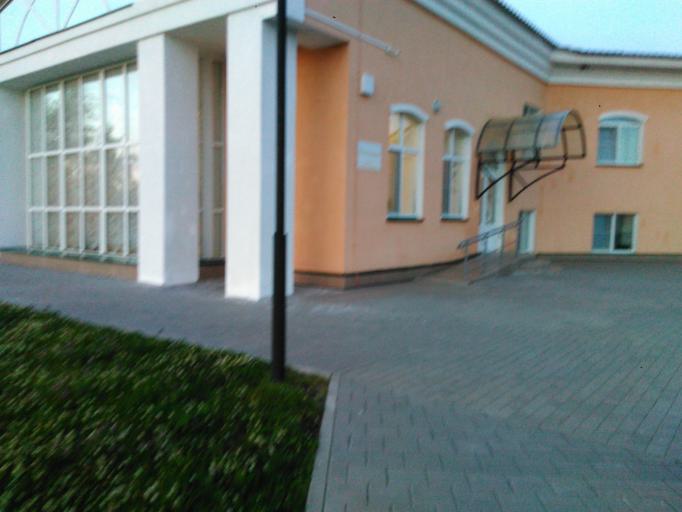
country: RU
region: Penza
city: Lermontovo
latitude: 53.0001
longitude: 43.6724
